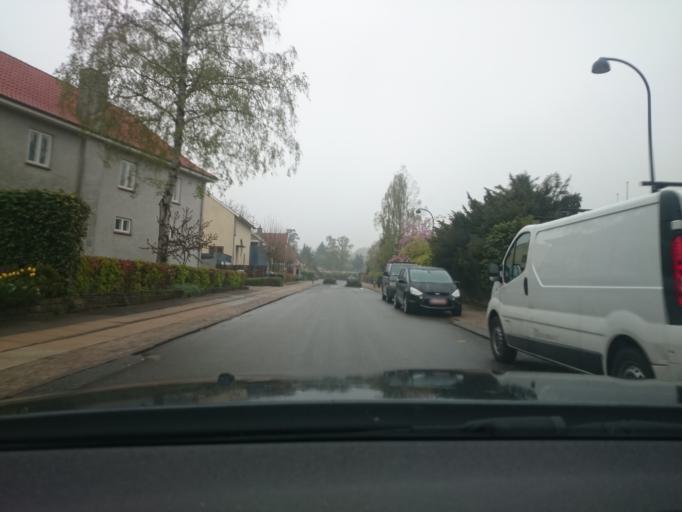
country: DK
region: Capital Region
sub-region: Gentofte Kommune
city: Charlottenlund
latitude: 55.7524
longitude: 12.5507
